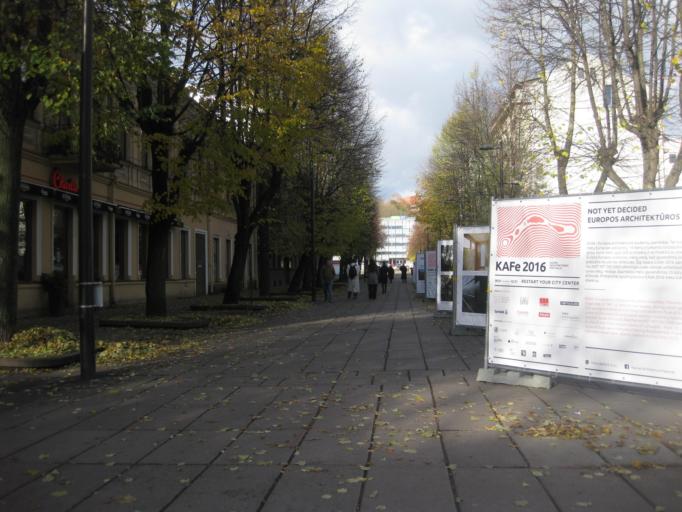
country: LT
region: Kauno apskritis
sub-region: Kaunas
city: Kaunas
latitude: 54.8975
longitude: 23.9136
